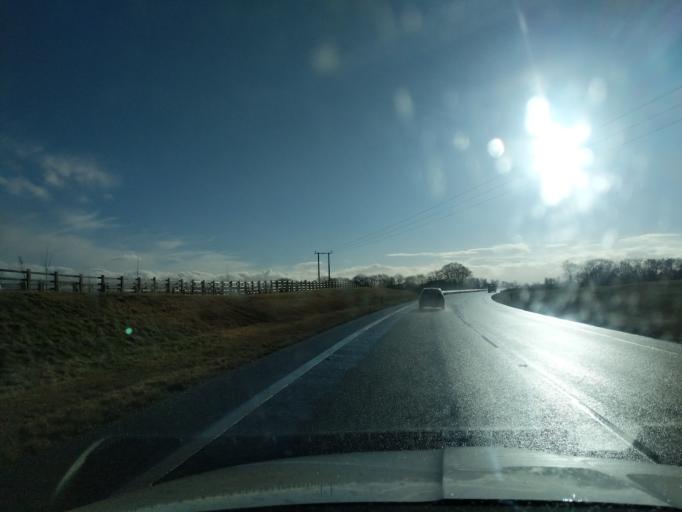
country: GB
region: England
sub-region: North Yorkshire
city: Bedale
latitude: 54.2977
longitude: -1.5895
